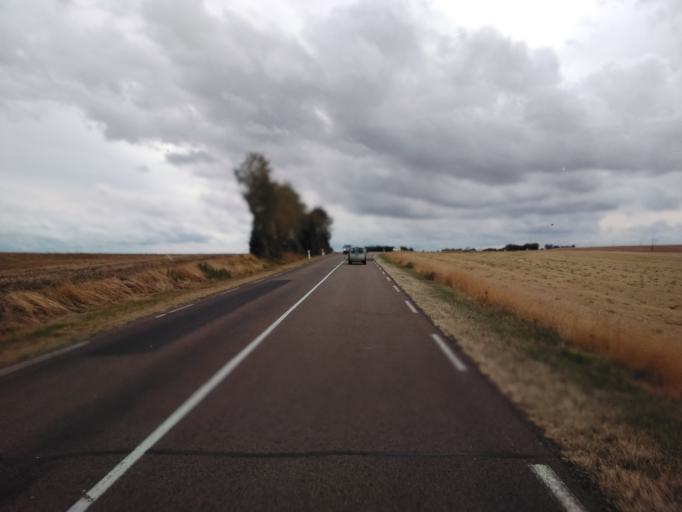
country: FR
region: Champagne-Ardenne
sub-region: Departement de la Marne
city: Frignicourt
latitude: 48.6161
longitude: 4.5686
